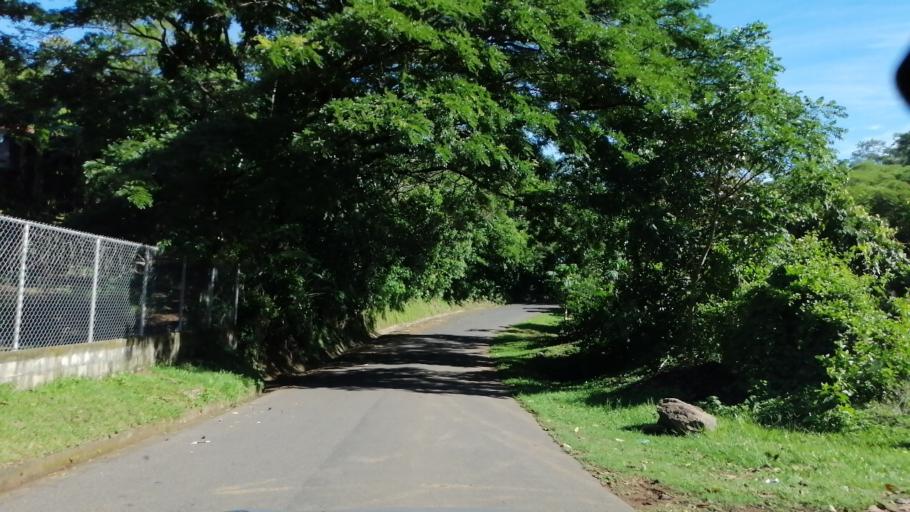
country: SV
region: Morazan
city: Corinto
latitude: 13.8014
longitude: -88.0036
